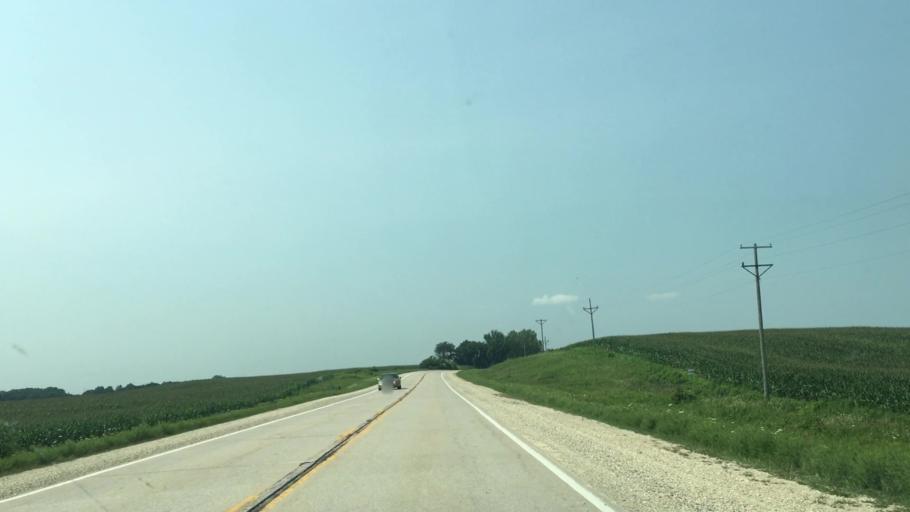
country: US
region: Iowa
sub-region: Fayette County
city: West Union
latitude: 43.0974
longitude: -91.8651
